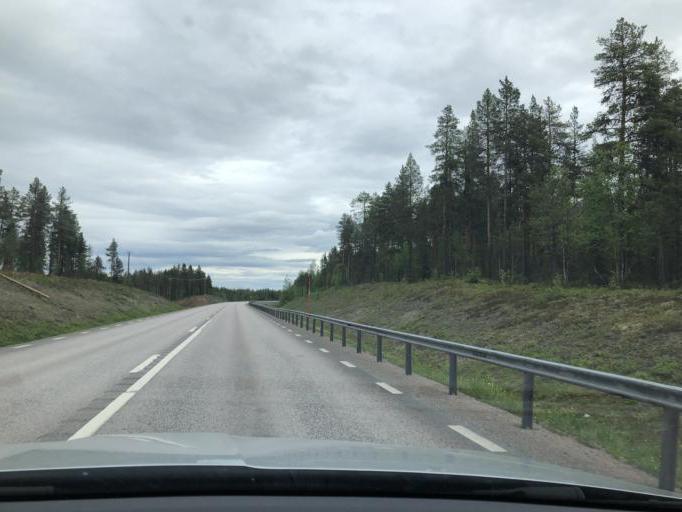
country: SE
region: Norrbotten
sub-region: Gallivare Kommun
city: Malmberget
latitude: 67.6430
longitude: 21.1048
